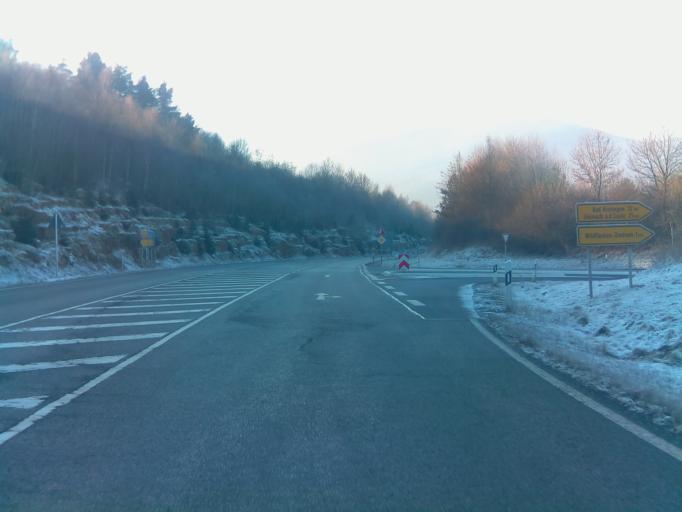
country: DE
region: Bavaria
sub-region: Regierungsbezirk Unterfranken
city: Wildflecken
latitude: 50.3736
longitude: 9.9123
